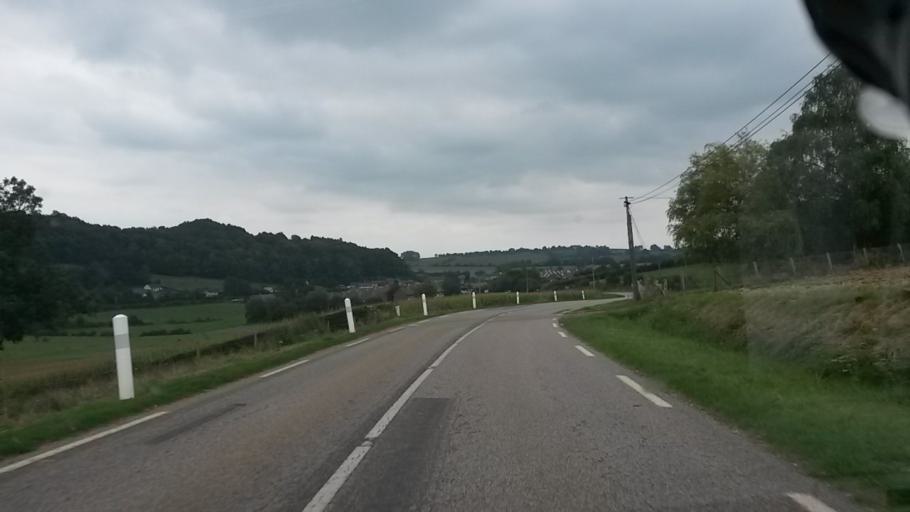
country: FR
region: Haute-Normandie
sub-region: Departement de la Seine-Maritime
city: Gaillefontaine
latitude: 49.6597
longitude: 1.6265
